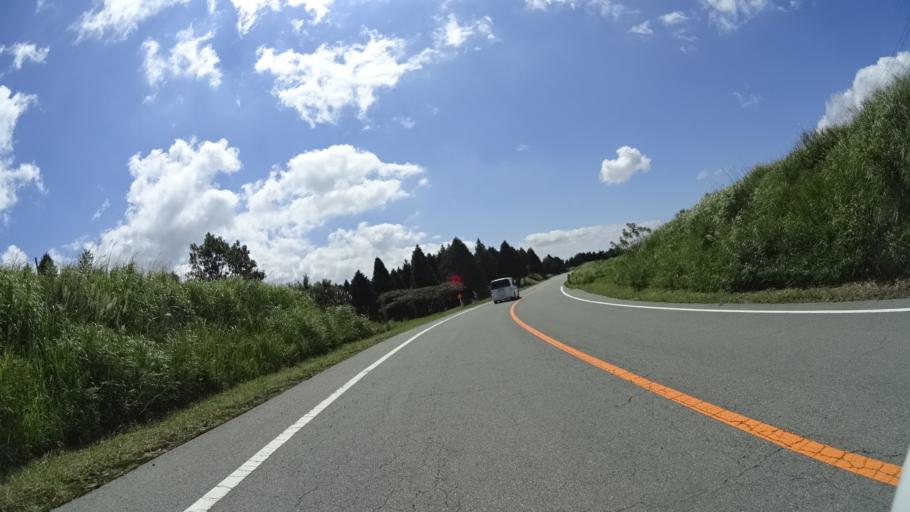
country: JP
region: Kumamoto
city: Aso
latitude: 33.0027
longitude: 131.0917
